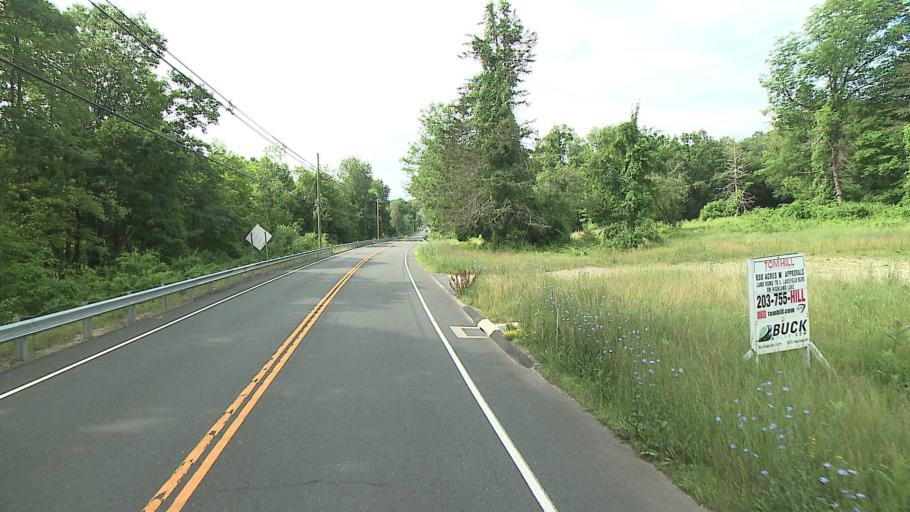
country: US
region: Connecticut
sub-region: Litchfield County
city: Winsted
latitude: 41.8863
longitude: -73.0745
